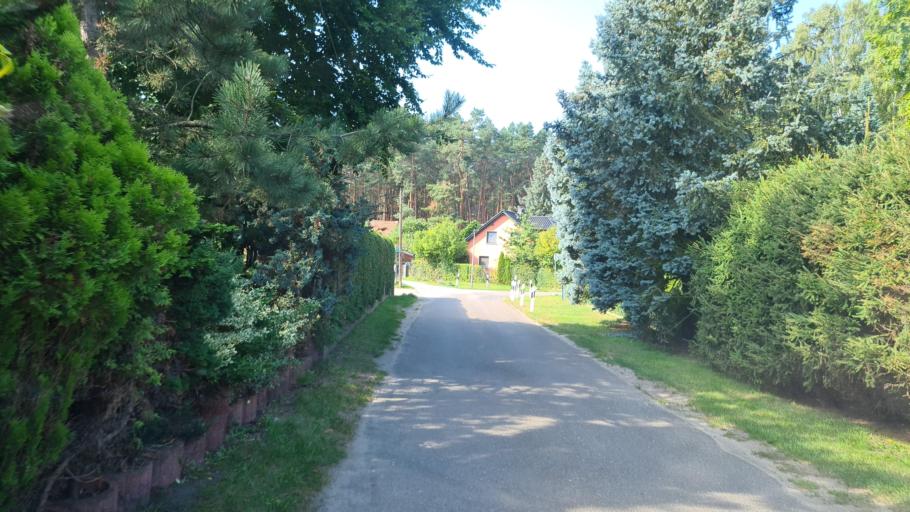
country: DE
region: Brandenburg
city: Kolkwitz
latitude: 51.7410
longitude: 14.2142
